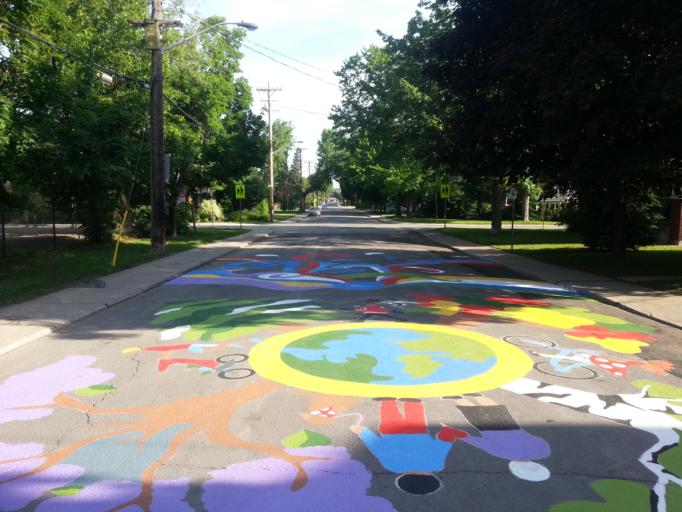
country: CA
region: Ontario
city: Ottawa
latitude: 45.3947
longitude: -75.7347
